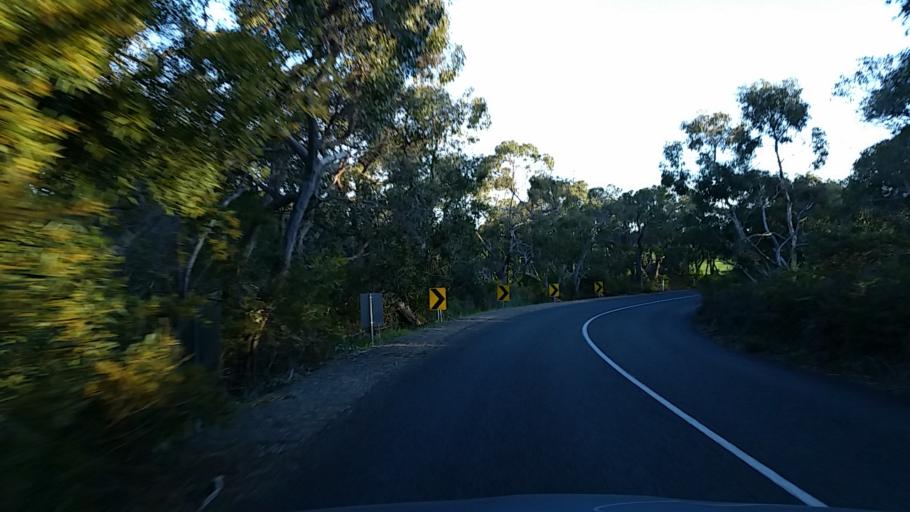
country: AU
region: South Australia
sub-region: Alexandrina
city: Mount Compass
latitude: -35.3279
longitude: 138.6634
